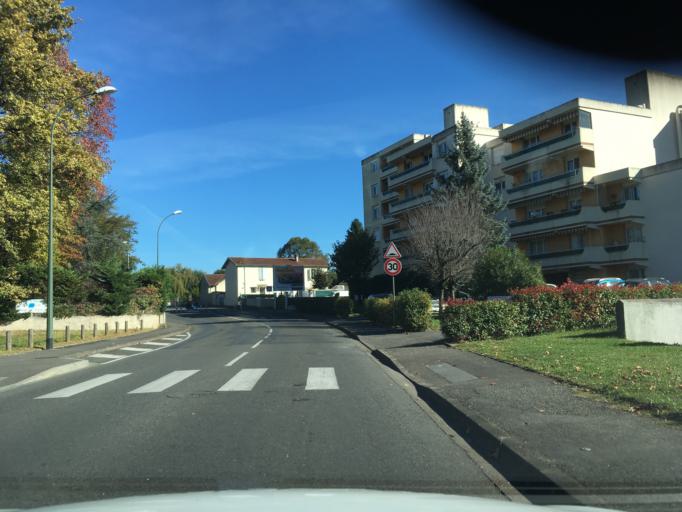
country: FR
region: Aquitaine
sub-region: Departement des Pyrenees-Atlantiques
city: Pau
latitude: 43.3152
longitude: -0.3539
